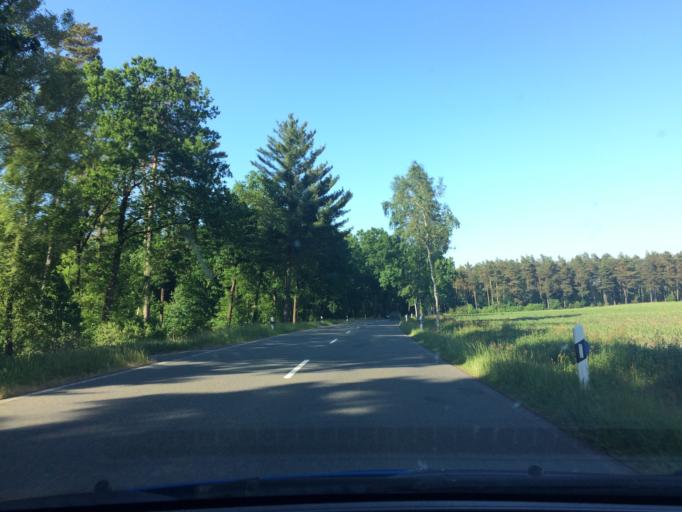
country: DE
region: Lower Saxony
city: Bispingen
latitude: 53.0459
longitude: 9.9365
